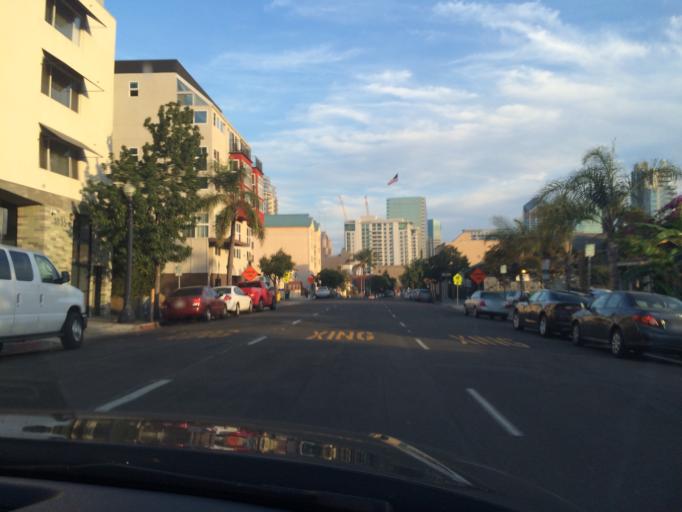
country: US
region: California
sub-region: San Diego County
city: San Diego
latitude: 32.7244
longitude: -117.1677
